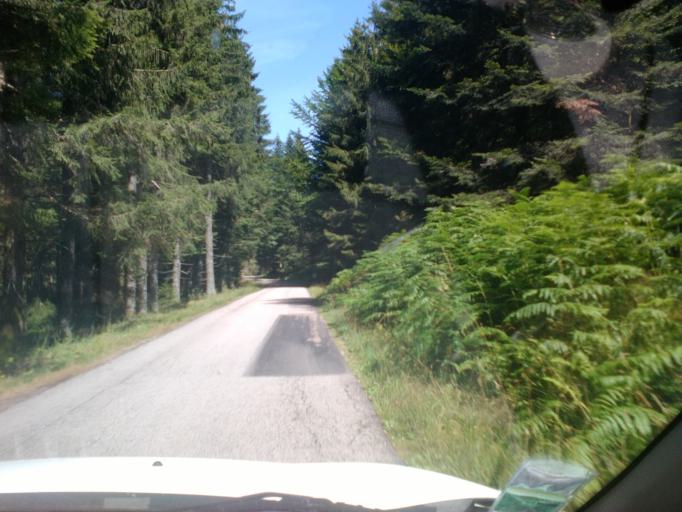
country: FR
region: Lorraine
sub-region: Departement des Vosges
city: Le Tholy
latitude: 48.0487
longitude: 6.7733
